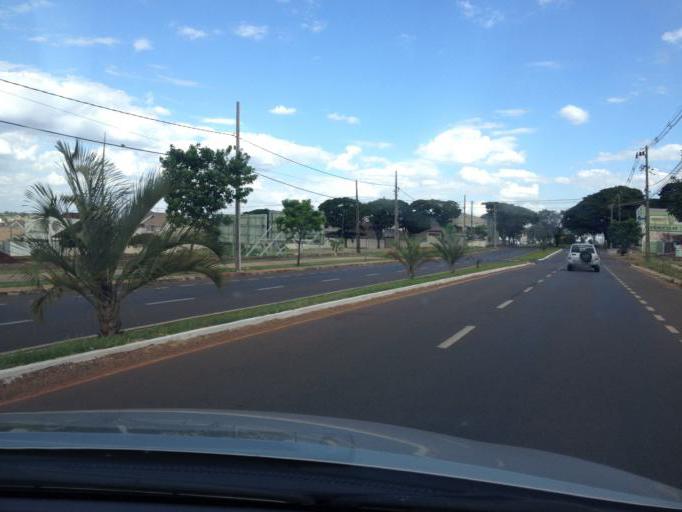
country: BR
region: Parana
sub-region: Maringa
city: Maringa
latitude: -23.4462
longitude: -51.9445
